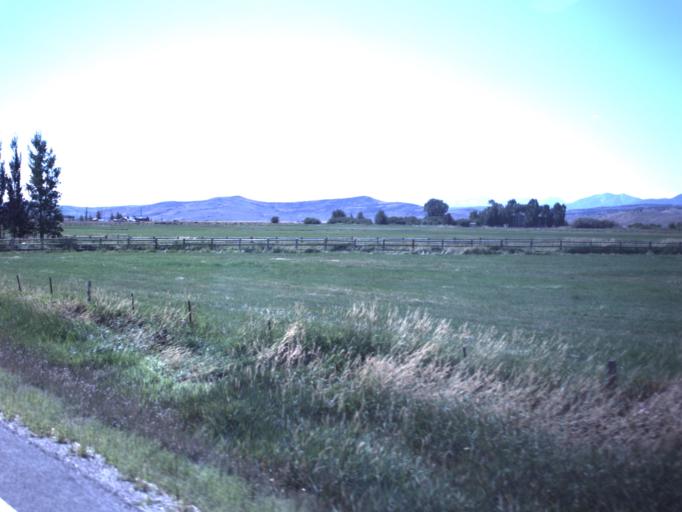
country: US
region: Utah
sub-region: Summit County
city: Kamas
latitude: 40.6636
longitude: -111.2808
